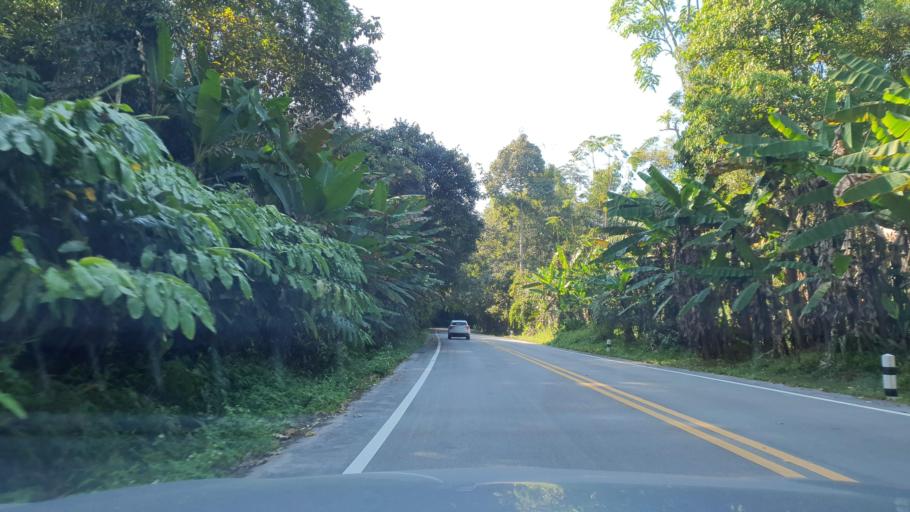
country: TH
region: Chiang Rai
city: Mae Lao
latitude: 19.8721
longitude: 99.6305
